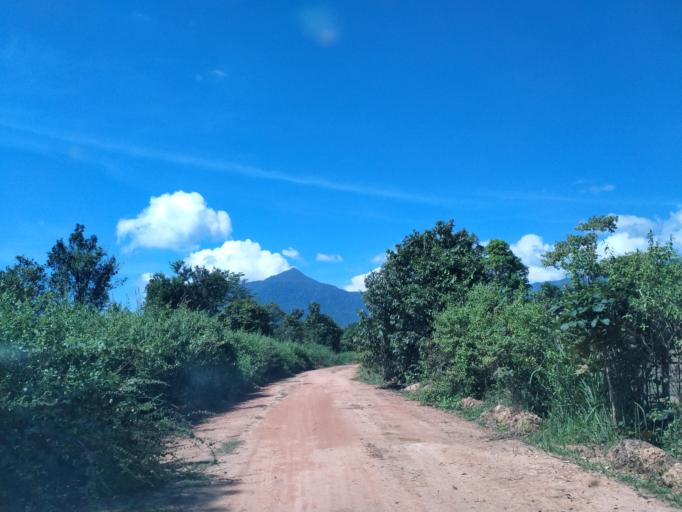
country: LA
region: Vientiane
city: Muang Phon-Hong
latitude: 18.6196
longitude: 102.8659
